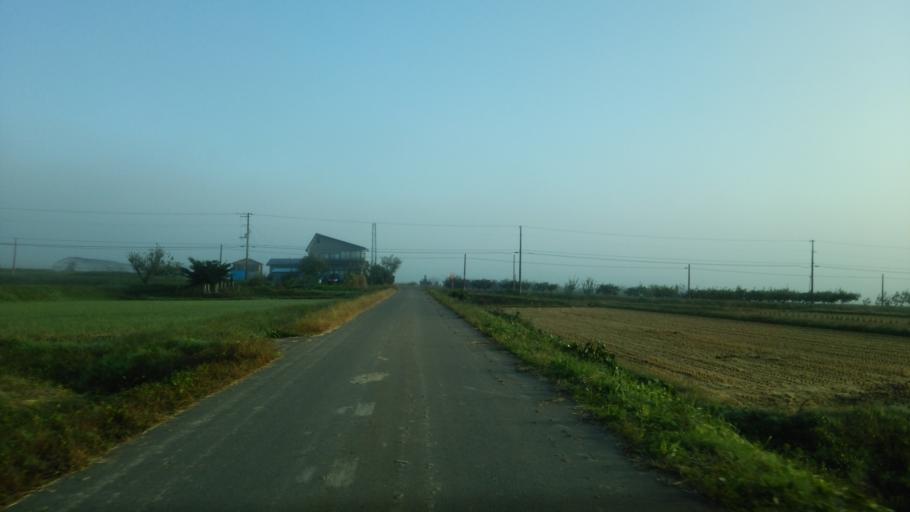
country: JP
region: Fukushima
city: Kitakata
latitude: 37.4448
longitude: 139.8064
